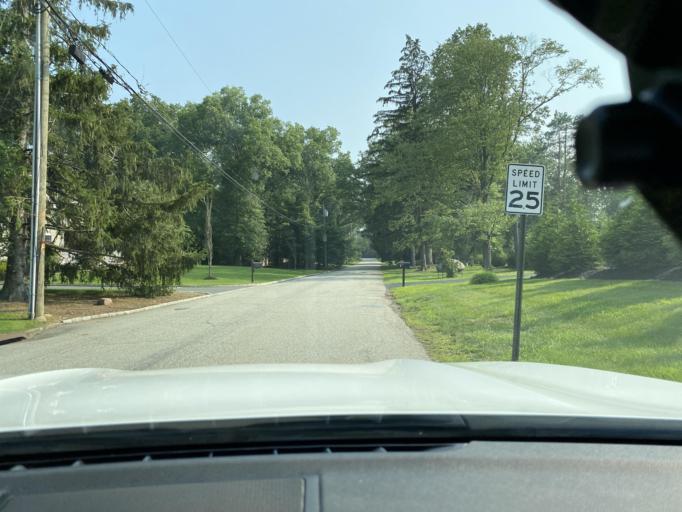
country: US
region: New York
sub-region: Rockland County
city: Airmont
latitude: 41.0841
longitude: -74.1177
